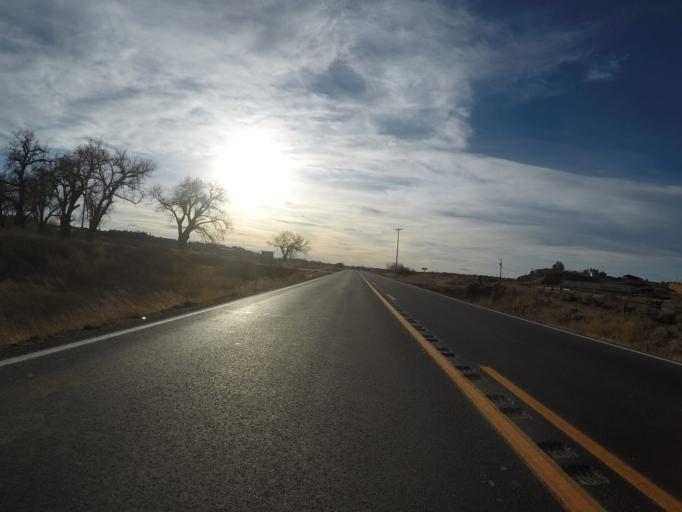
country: US
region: Montana
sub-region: Musselshell County
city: Roundup
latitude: 46.3667
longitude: -108.6515
